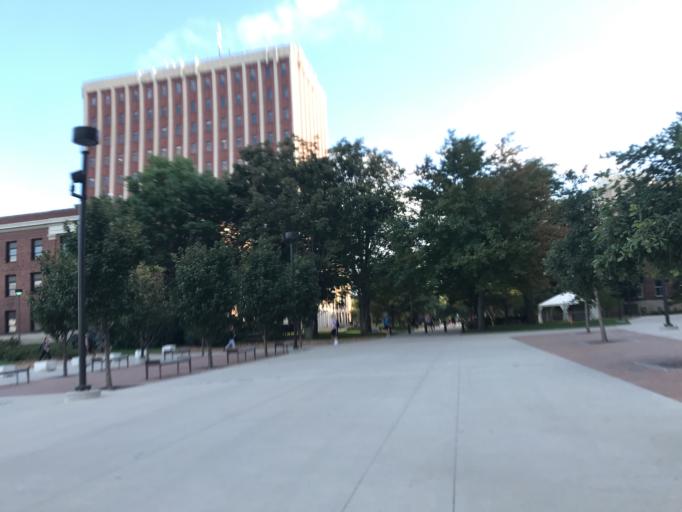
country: US
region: Nebraska
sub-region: Lancaster County
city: Lincoln
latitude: 40.8207
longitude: -96.7041
